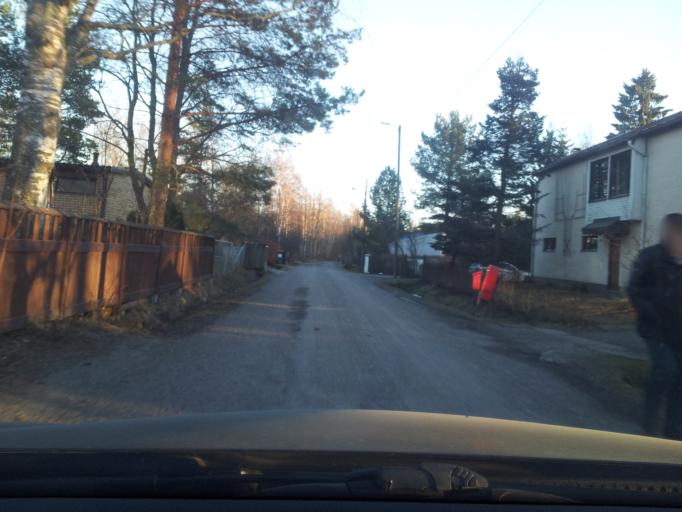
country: FI
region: Uusimaa
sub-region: Helsinki
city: Kauniainen
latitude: 60.1683
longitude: 24.7233
